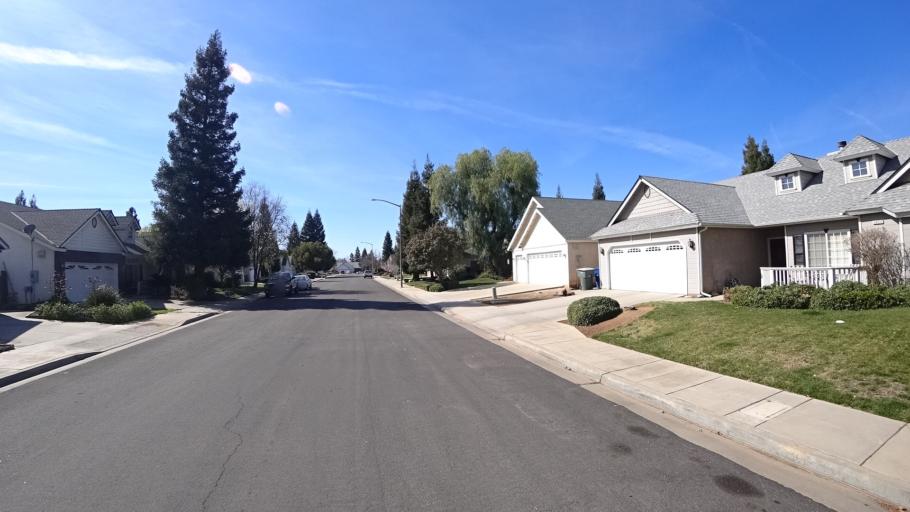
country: US
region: California
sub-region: Fresno County
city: Clovis
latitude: 36.8495
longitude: -119.7359
